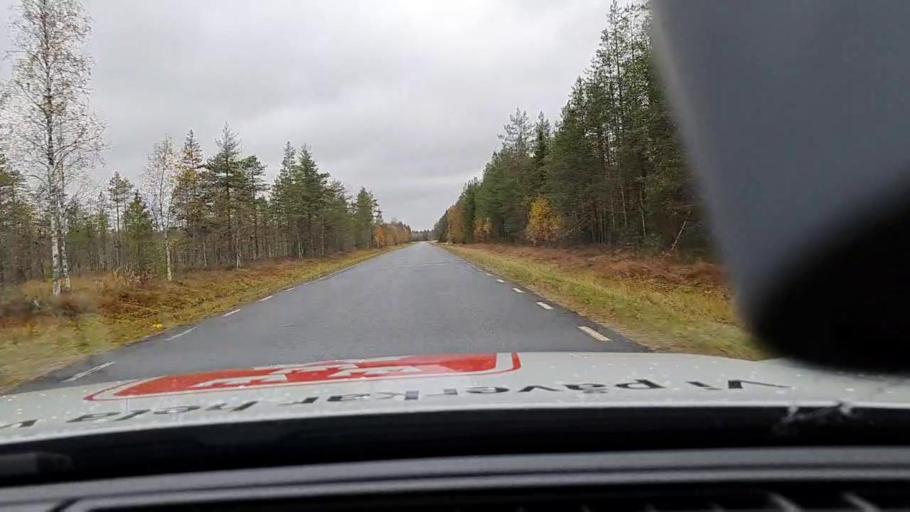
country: SE
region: Norrbotten
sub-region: Haparanda Kommun
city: Haparanda
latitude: 65.9265
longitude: 23.8192
